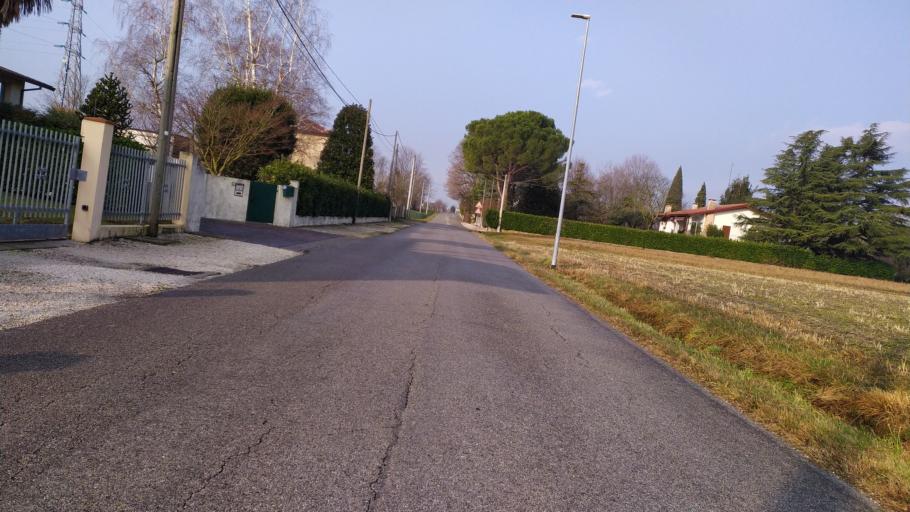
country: IT
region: Friuli Venezia Giulia
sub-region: Provincia di Pordenone
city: Caneva
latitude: 45.9495
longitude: 12.4575
